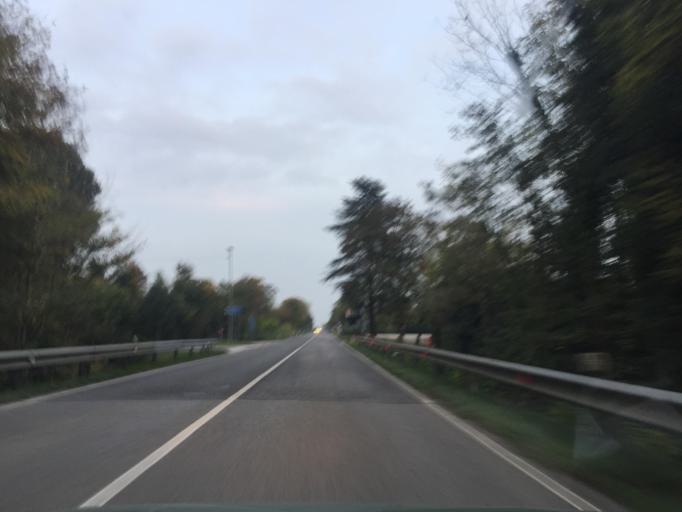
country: IT
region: Friuli Venezia Giulia
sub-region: Provincia di Pordenone
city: Fanna
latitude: 46.1690
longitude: 12.7602
